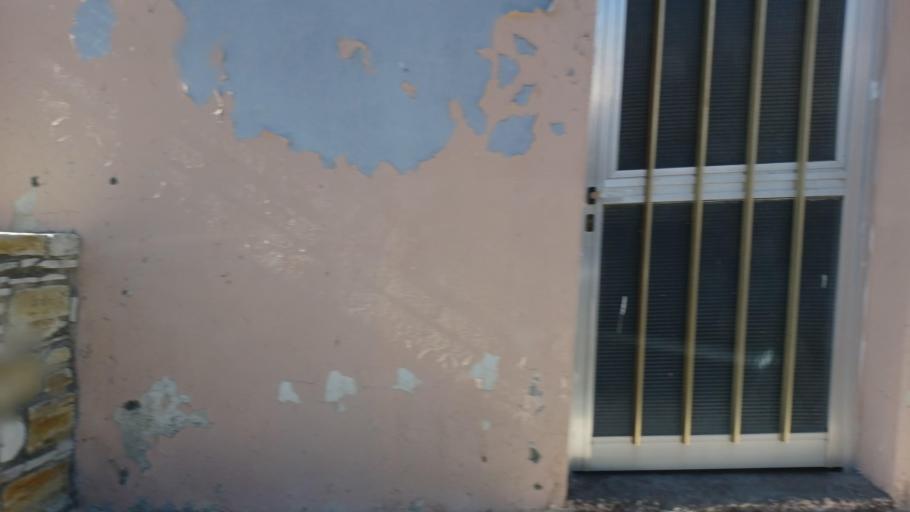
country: CY
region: Limassol
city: Pyrgos
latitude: 34.7791
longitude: 33.2557
